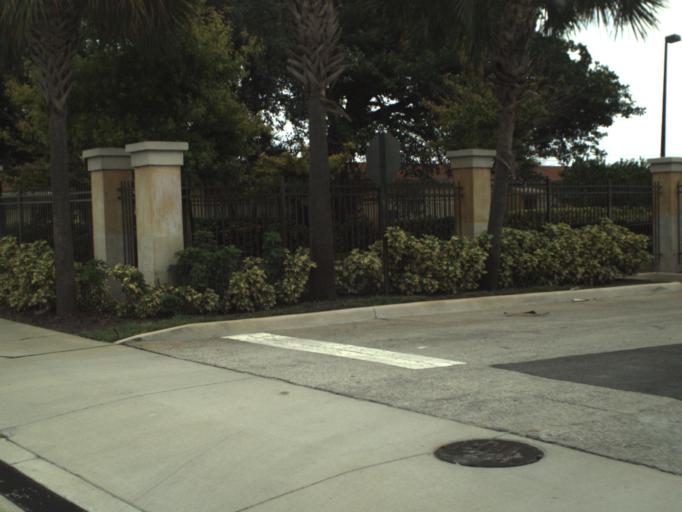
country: US
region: Florida
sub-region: Palm Beach County
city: Riviera Beach
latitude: 26.7890
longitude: -80.0544
